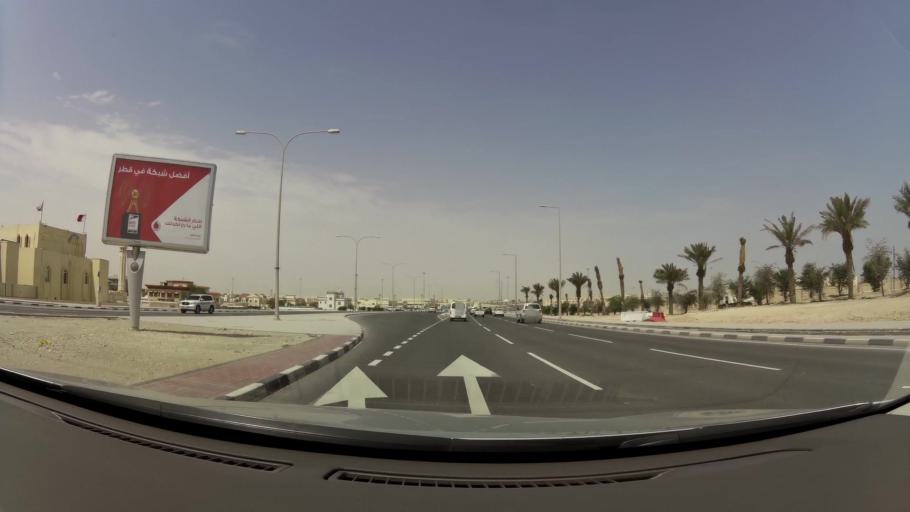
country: QA
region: Baladiyat ar Rayyan
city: Ar Rayyan
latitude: 25.3466
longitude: 51.4794
